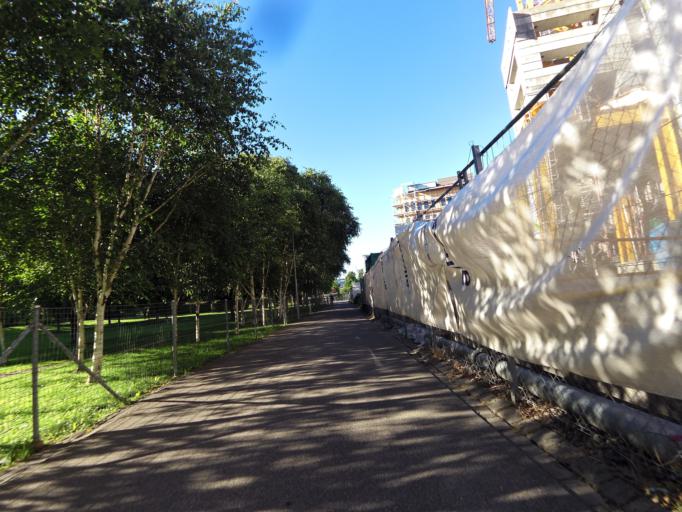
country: CH
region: Zurich
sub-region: Bezirk Zuerich
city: Zuerich (Kreis 9) / Albisrieden
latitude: 47.3808
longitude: 8.4872
